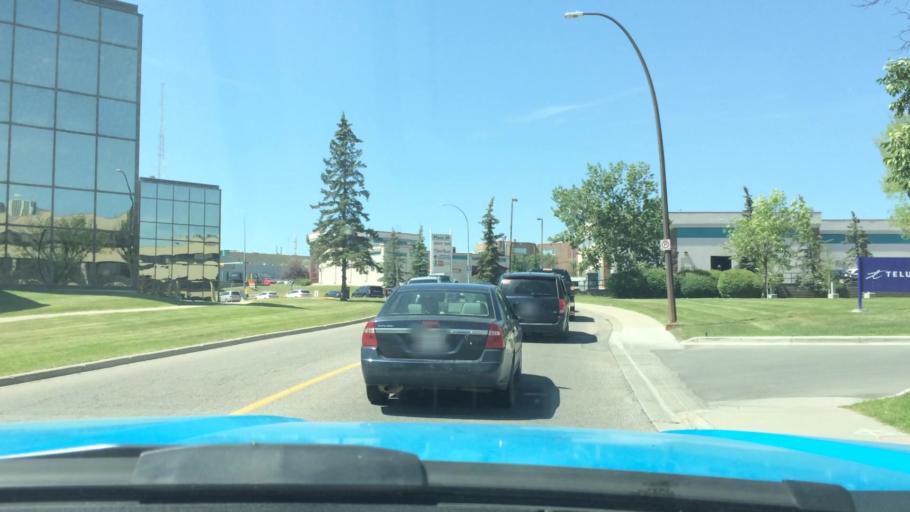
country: CA
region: Alberta
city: Calgary
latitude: 51.0504
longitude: -113.9903
